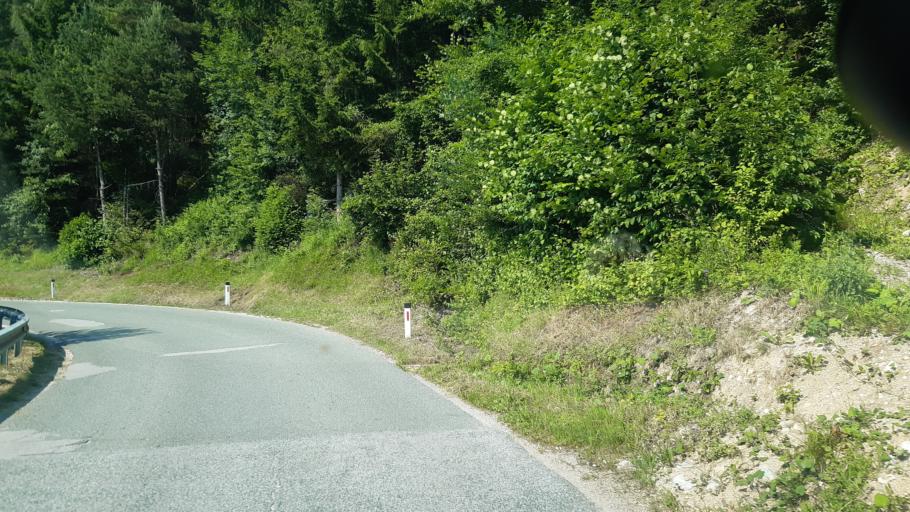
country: SI
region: Trzic
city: Bistrica pri Trzicu
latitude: 46.3601
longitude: 14.2639
